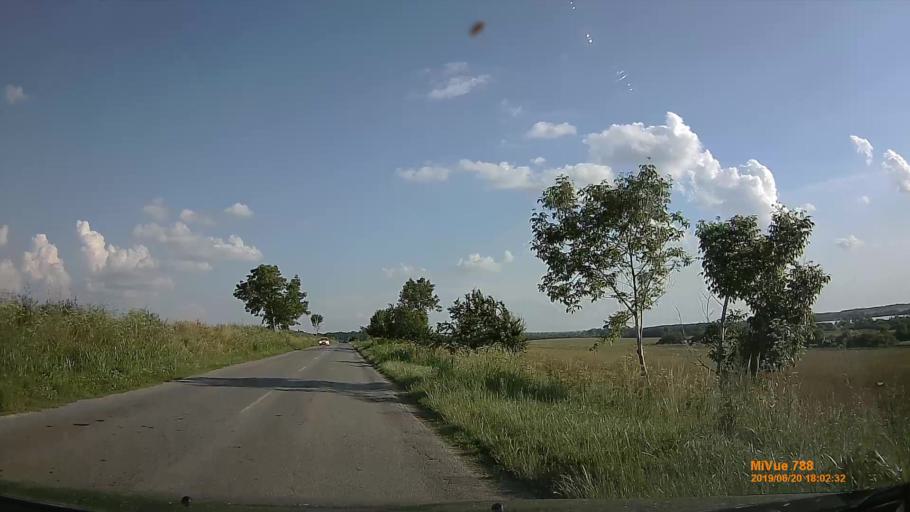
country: HU
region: Baranya
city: Szentlorinc
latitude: 46.0735
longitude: 17.9907
